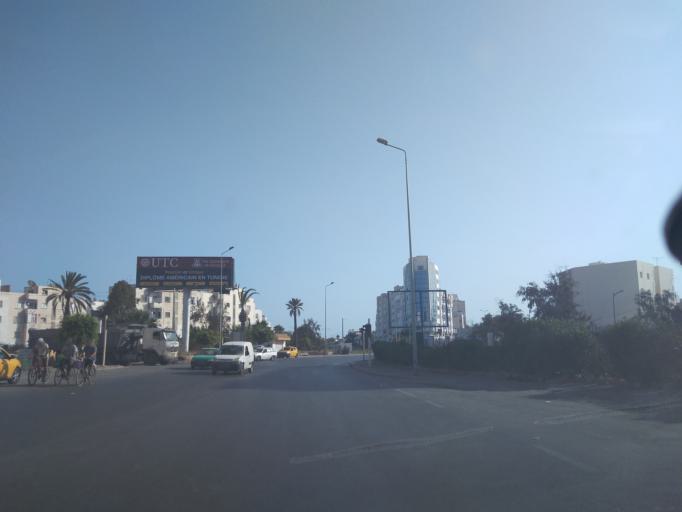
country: TN
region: Safaqis
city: Sfax
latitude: 34.7453
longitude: 10.7655
